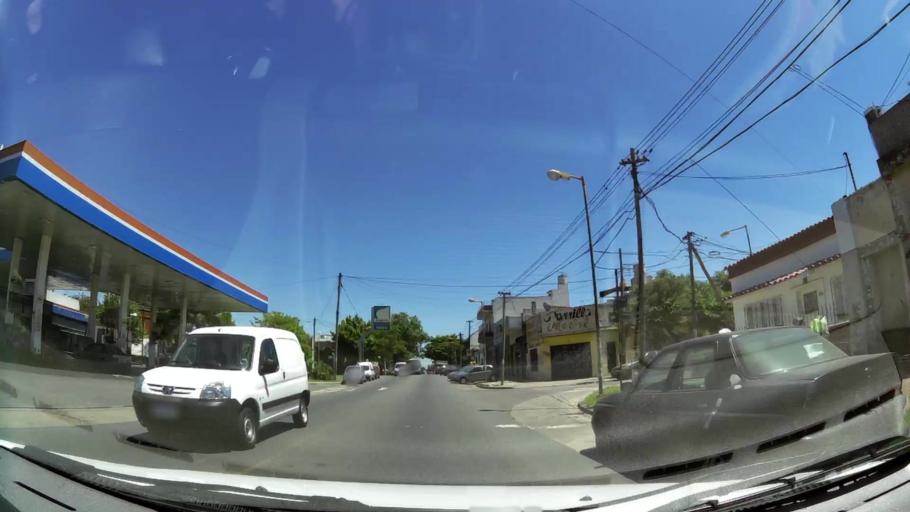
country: AR
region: Buenos Aires
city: Caseros
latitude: -34.5888
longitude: -58.5552
